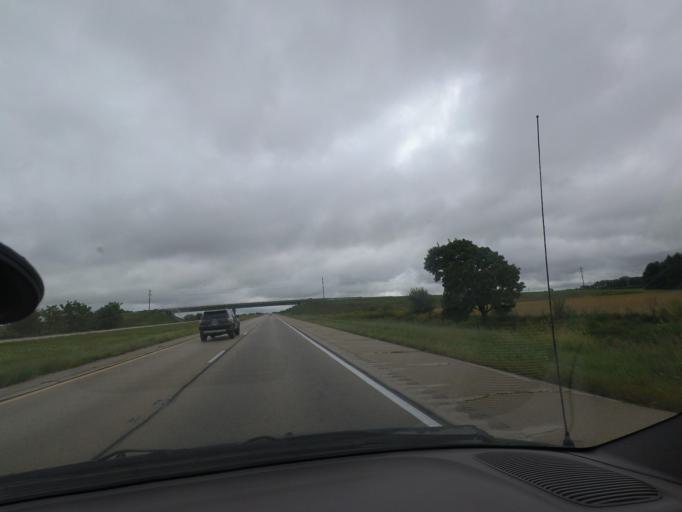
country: US
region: Illinois
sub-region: Piatt County
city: Monticello
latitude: 40.0232
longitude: -88.6902
